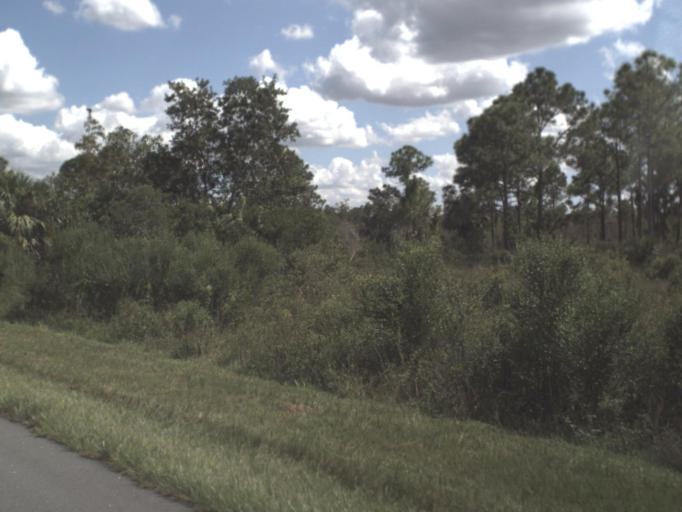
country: US
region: Florida
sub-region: Collier County
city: Marco
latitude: 25.8712
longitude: -81.1745
